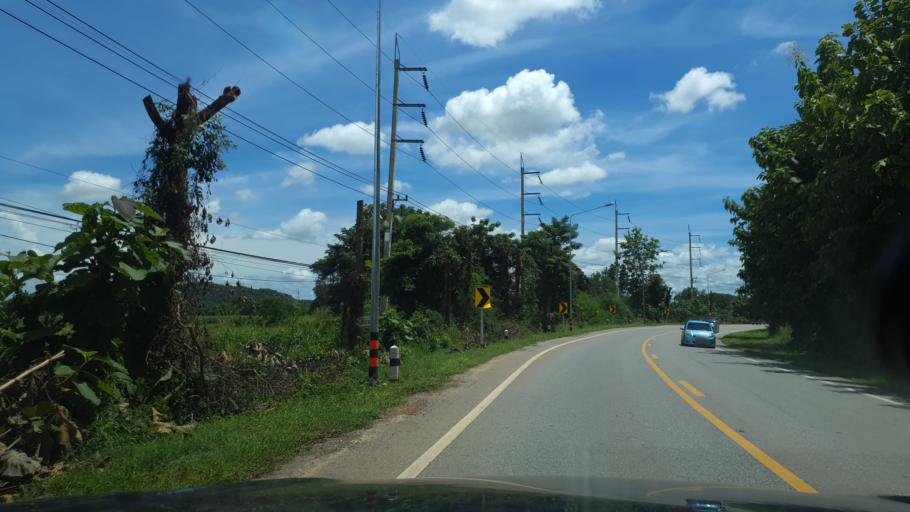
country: TH
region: Sukhothai
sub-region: Amphoe Si Satchanalai
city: Si Satchanalai
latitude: 17.4596
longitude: 99.7848
